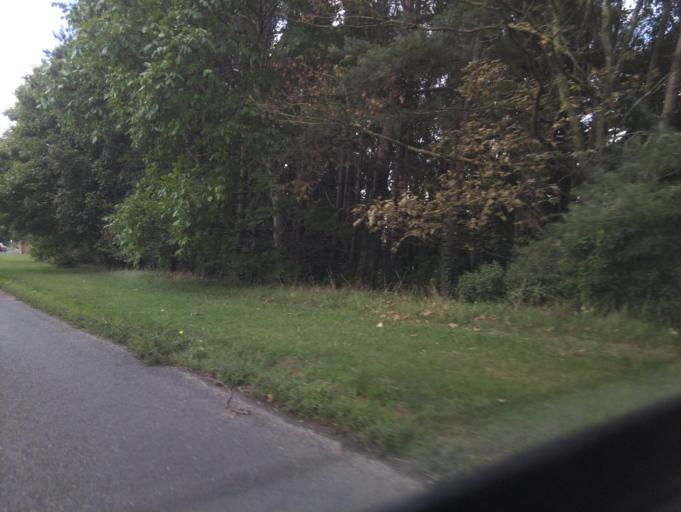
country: GB
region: England
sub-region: North Yorkshire
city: Ripon
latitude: 54.1912
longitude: -1.5665
